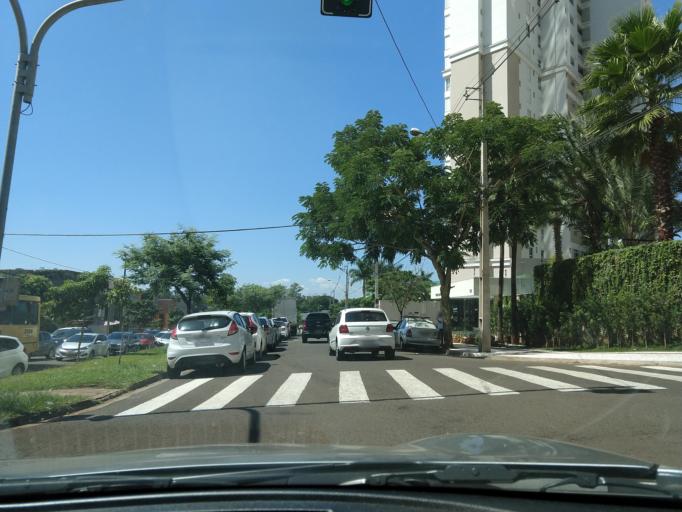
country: BR
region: Parana
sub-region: Londrina
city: Londrina
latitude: -23.3306
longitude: -51.1743
